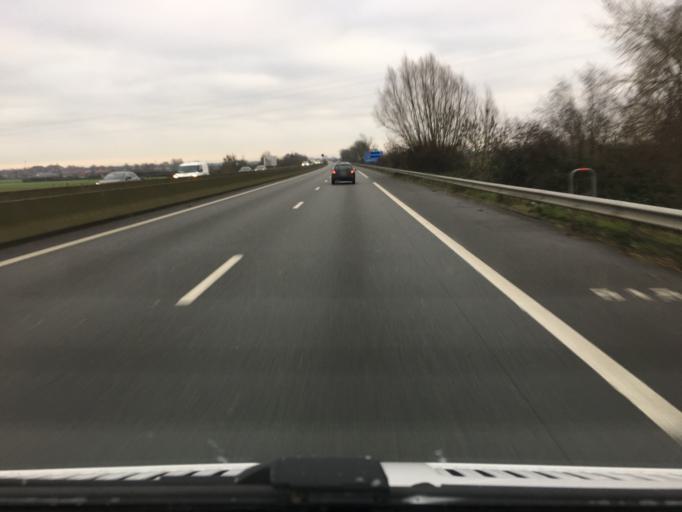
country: FR
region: Nord-Pas-de-Calais
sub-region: Departement du Nord
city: Meteren
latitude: 50.7302
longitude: 2.7056
